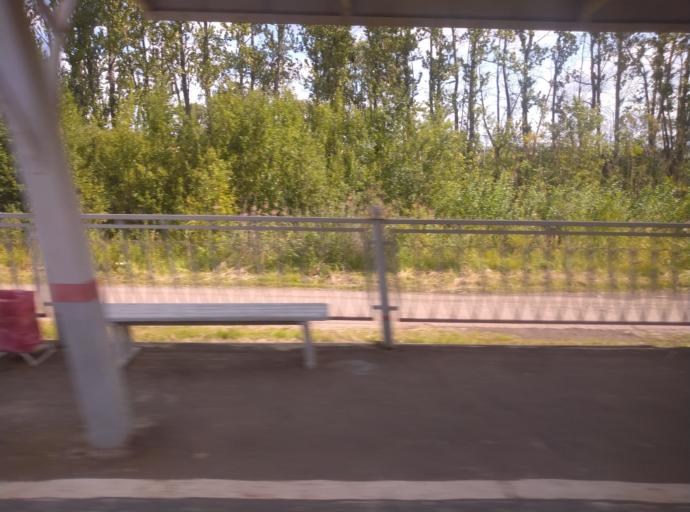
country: RU
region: St.-Petersburg
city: Obukhovo
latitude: 59.8796
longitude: 30.4072
